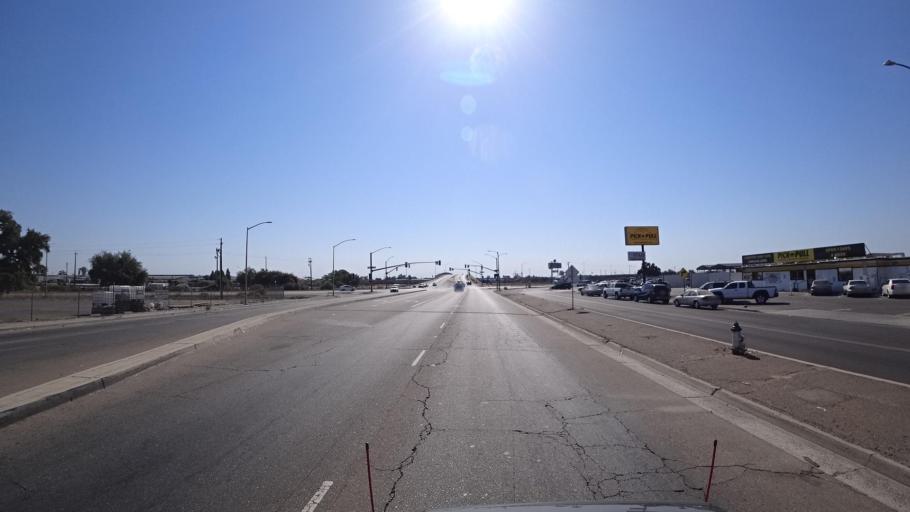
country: US
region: California
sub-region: Fresno County
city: Fresno
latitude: 36.7068
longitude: -119.7699
